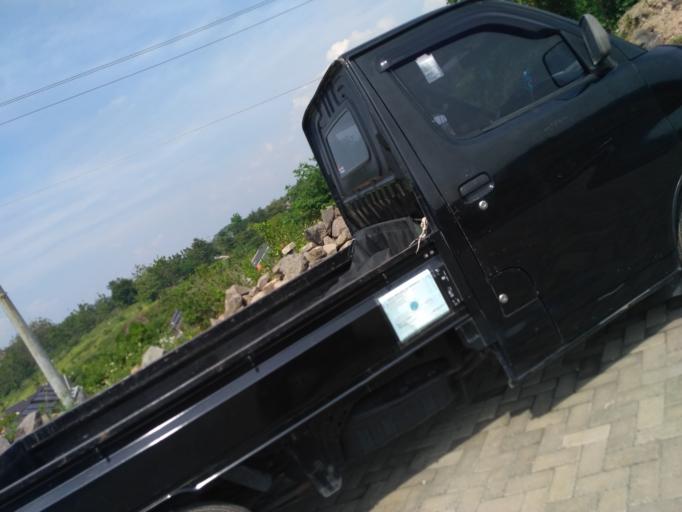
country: ID
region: Central Java
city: Semarang
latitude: -7.0375
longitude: 110.4383
